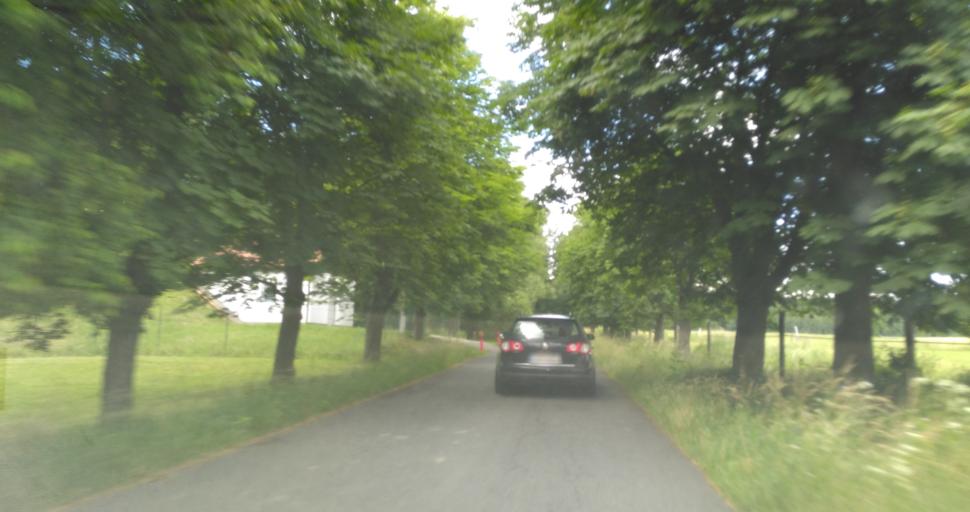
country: CZ
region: Plzensky
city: Zbiroh
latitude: 49.8924
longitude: 13.8062
